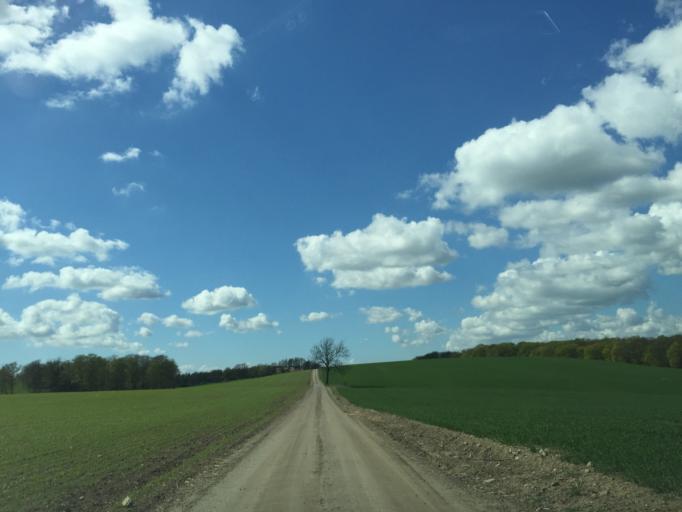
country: SE
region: Skane
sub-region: Lunds Kommun
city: Genarp
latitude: 55.7045
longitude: 13.3671
